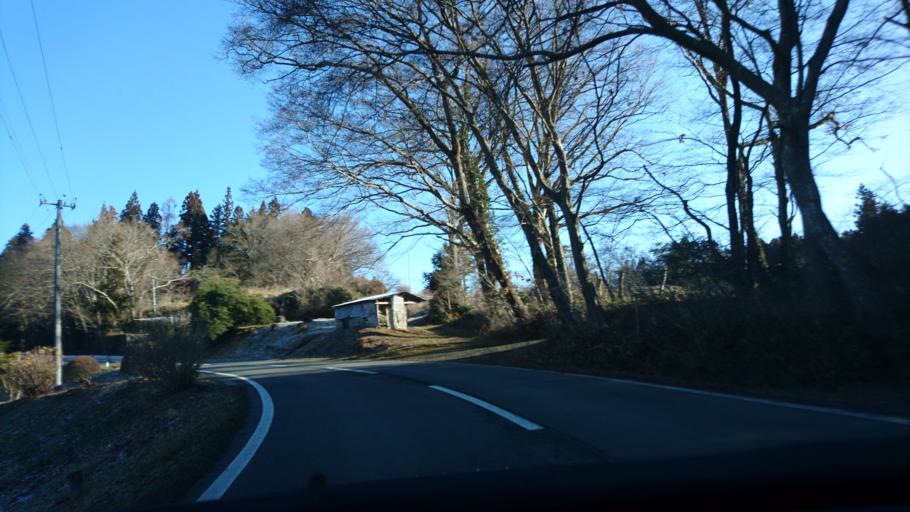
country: JP
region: Iwate
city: Ichinoseki
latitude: 38.8602
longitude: 141.2992
